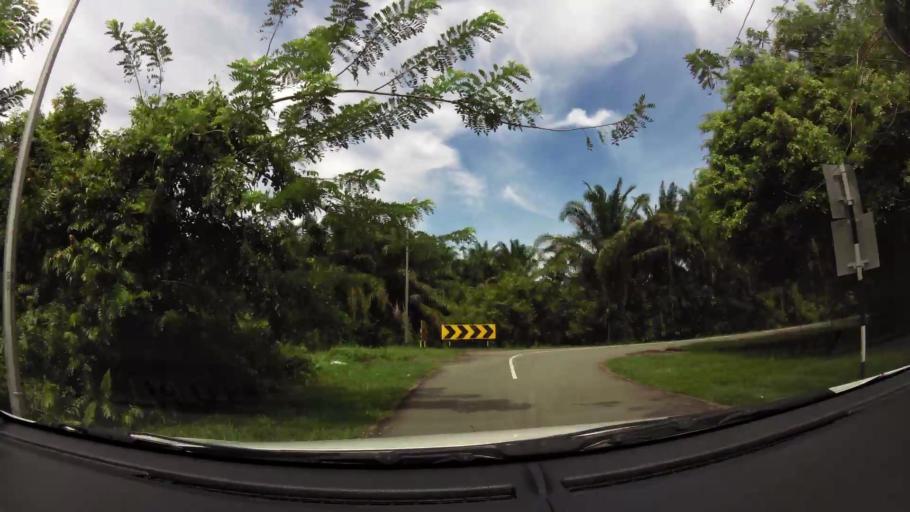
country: BN
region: Belait
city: Seria
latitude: 4.5973
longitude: 114.2873
